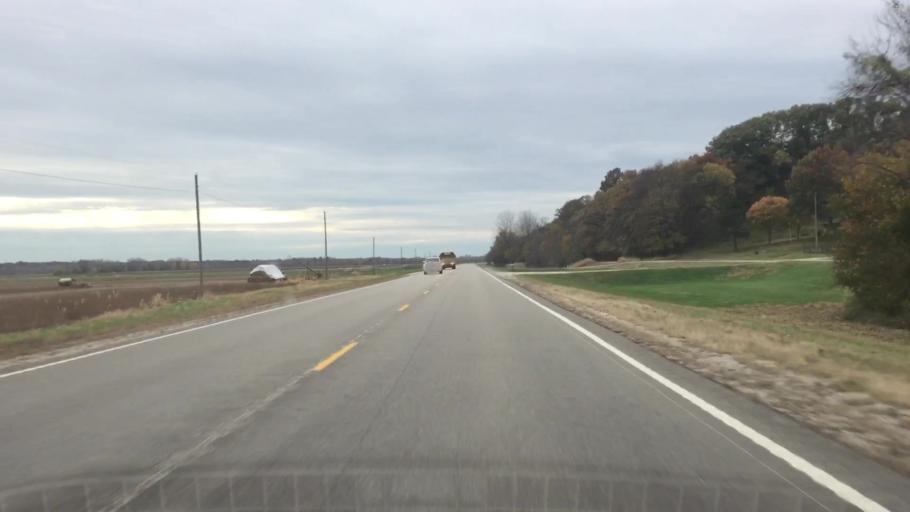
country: US
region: Missouri
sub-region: Callaway County
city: Holts Summit
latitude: 38.5807
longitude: -92.0843
